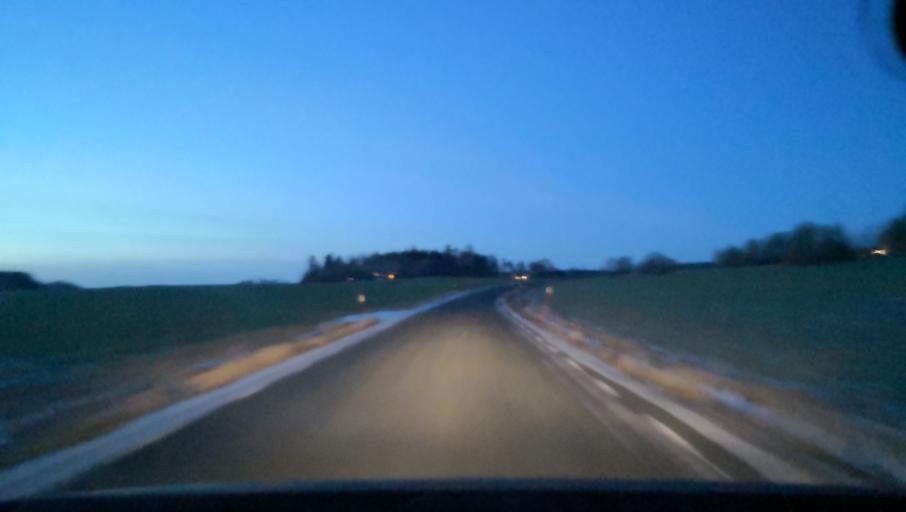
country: SE
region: Soedermanland
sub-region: Katrineholms Kommun
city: Katrineholm
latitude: 59.0781
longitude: 16.3425
